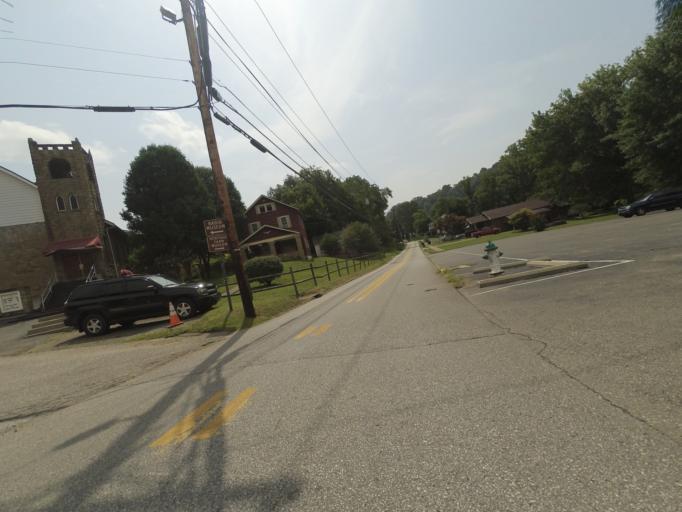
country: US
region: West Virginia
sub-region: Cabell County
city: Huntington
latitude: 38.4016
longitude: -82.4747
